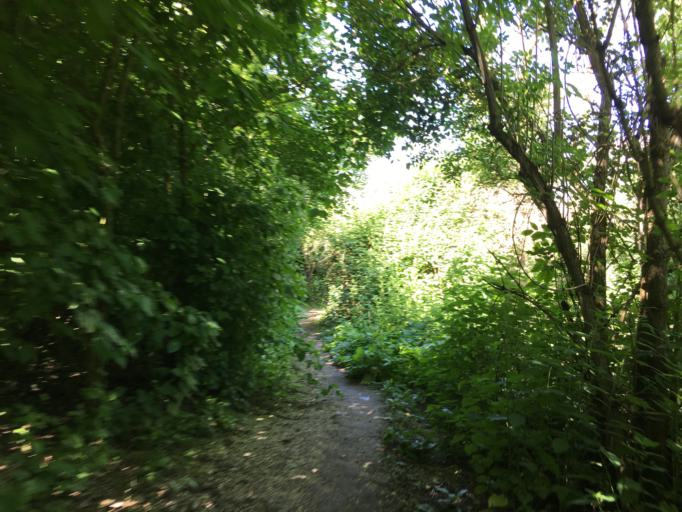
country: GB
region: England
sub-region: Warwickshire
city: Rugby
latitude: 52.3901
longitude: -1.2559
